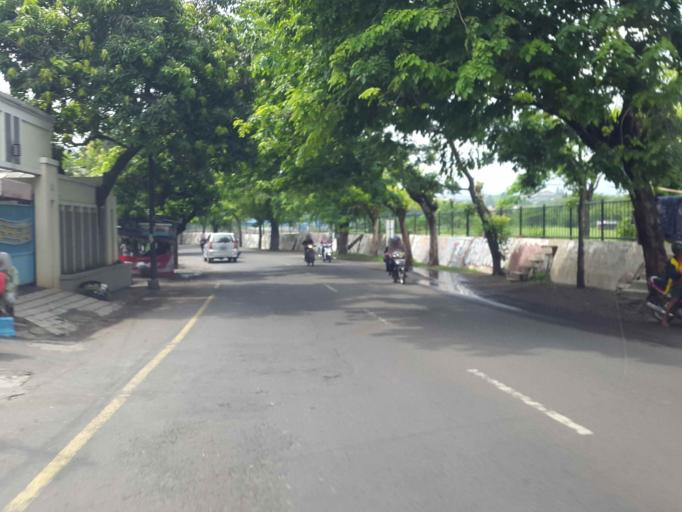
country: ID
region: Central Java
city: Semarang
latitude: -6.9983
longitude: 110.4015
